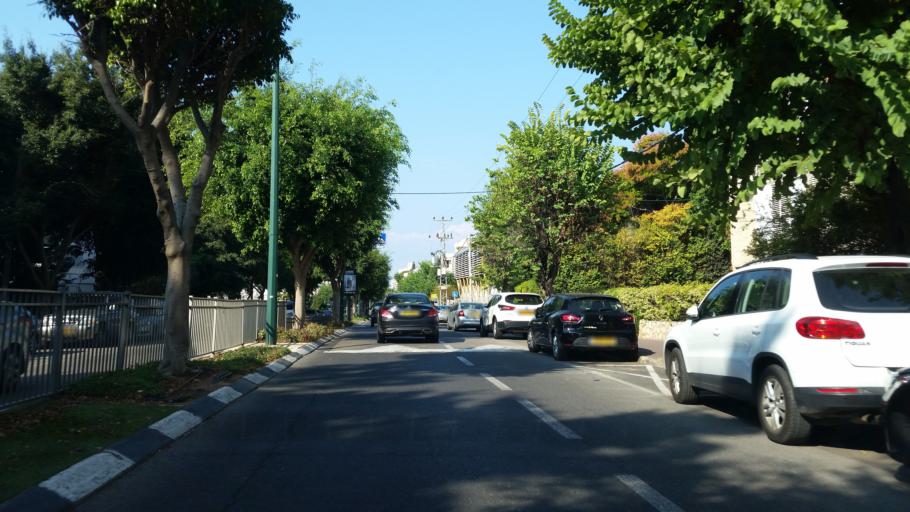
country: IL
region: Tel Aviv
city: Herzliyya
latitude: 32.1616
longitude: 34.8400
